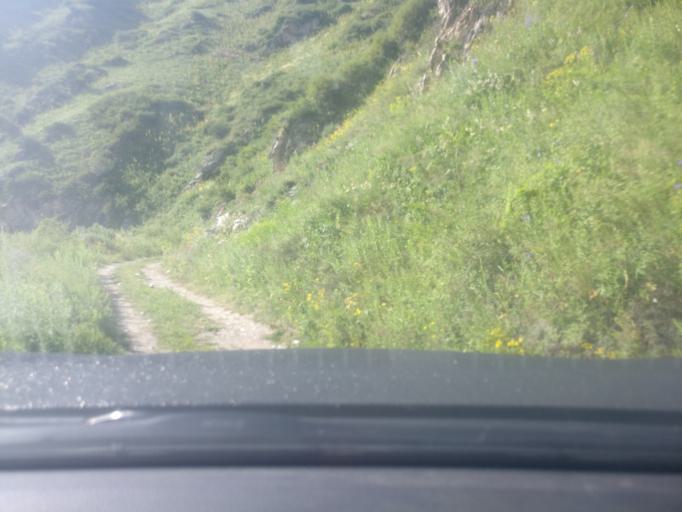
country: KZ
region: Almaty Qalasy
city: Almaty
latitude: 43.1075
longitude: 76.9408
